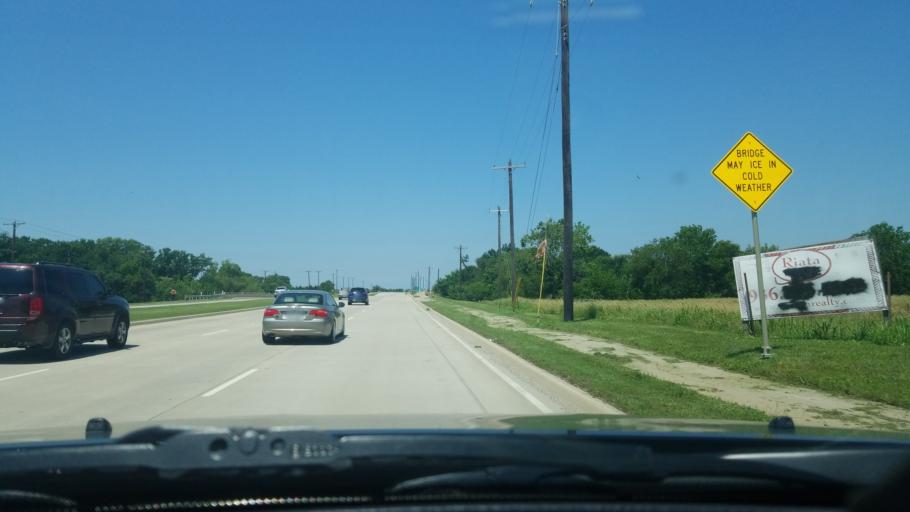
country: US
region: Texas
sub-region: Denton County
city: Krum
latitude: 33.2317
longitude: -97.2157
